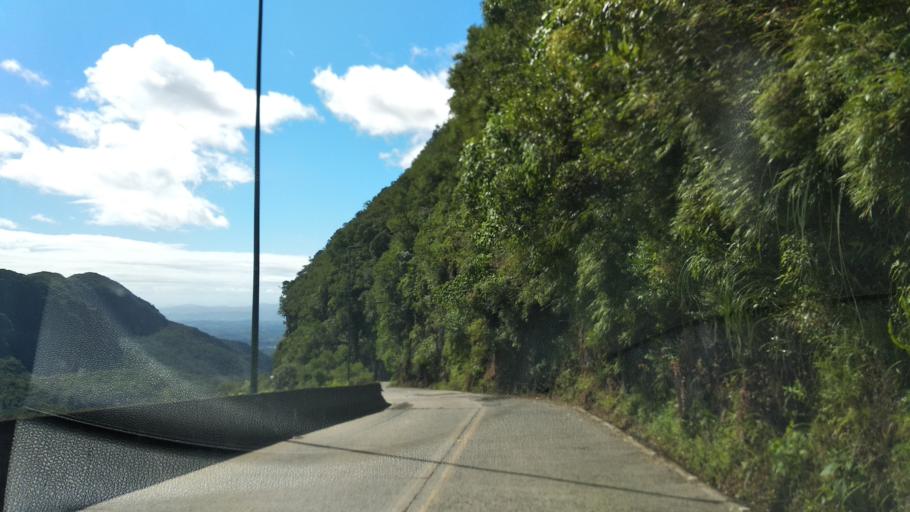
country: BR
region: Santa Catarina
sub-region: Lauro Muller
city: Lauro Muller
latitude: -28.3929
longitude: -49.5347
